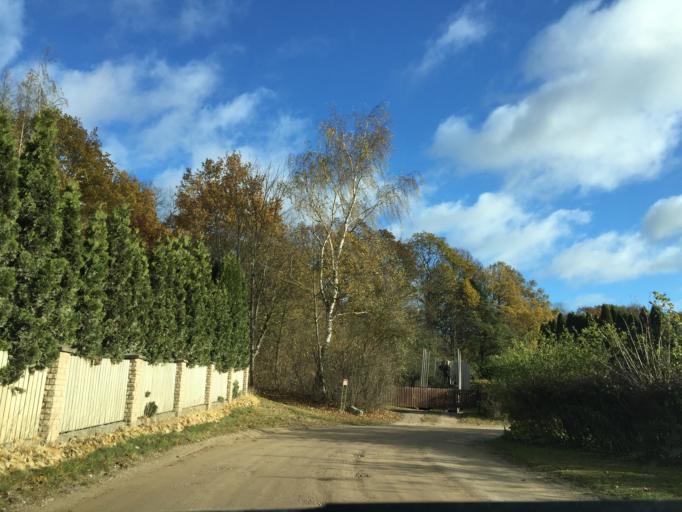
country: LV
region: Tukuma Rajons
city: Tukums
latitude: 56.9711
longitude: 23.1752
